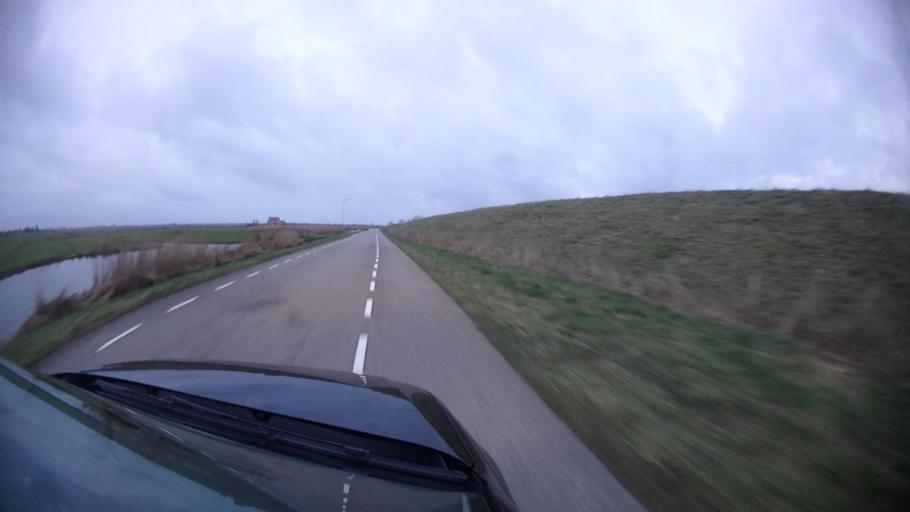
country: NL
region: North Holland
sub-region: Gemeente Edam-Volendam
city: Volendam
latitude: 52.4743
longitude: 5.0644
